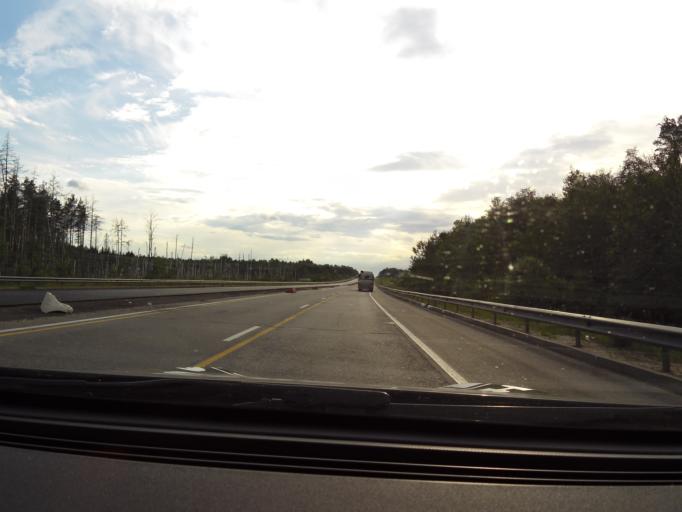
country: RU
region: Vladimir
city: Orgtrud
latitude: 56.1024
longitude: 40.7640
